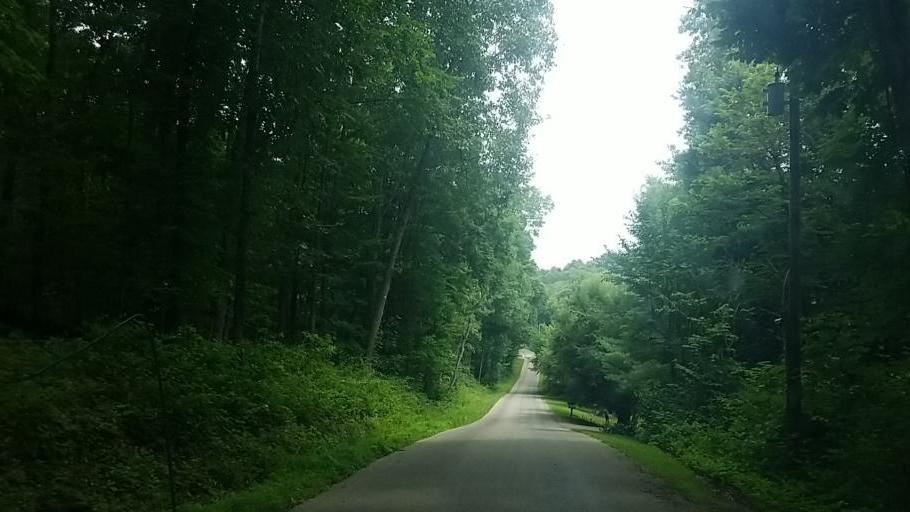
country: US
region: Ohio
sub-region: Licking County
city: Utica
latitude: 40.2460
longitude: -82.2935
